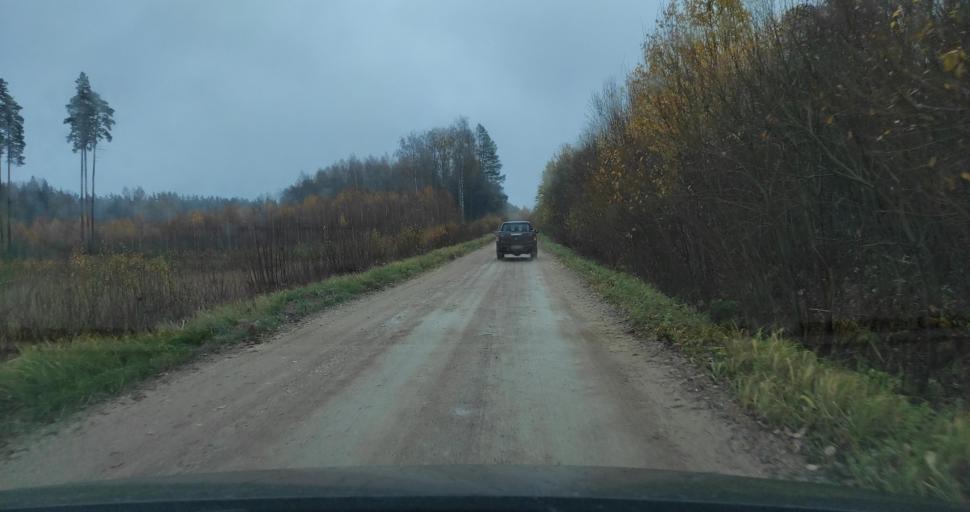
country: LV
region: Skrunda
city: Skrunda
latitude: 56.6949
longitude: 22.1098
